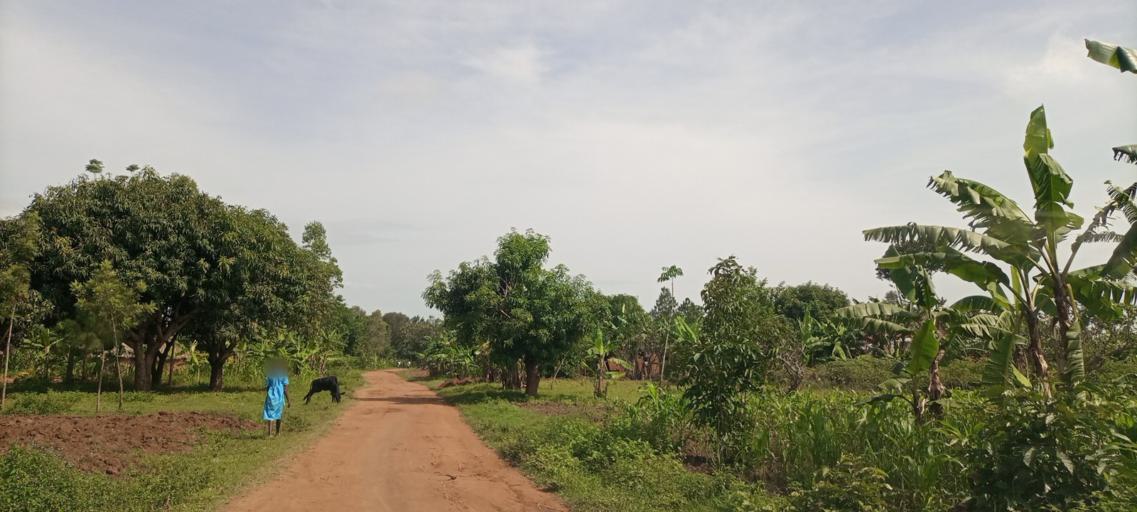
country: UG
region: Eastern Region
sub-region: Mbale District
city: Mbale
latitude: 1.1267
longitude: 34.0283
